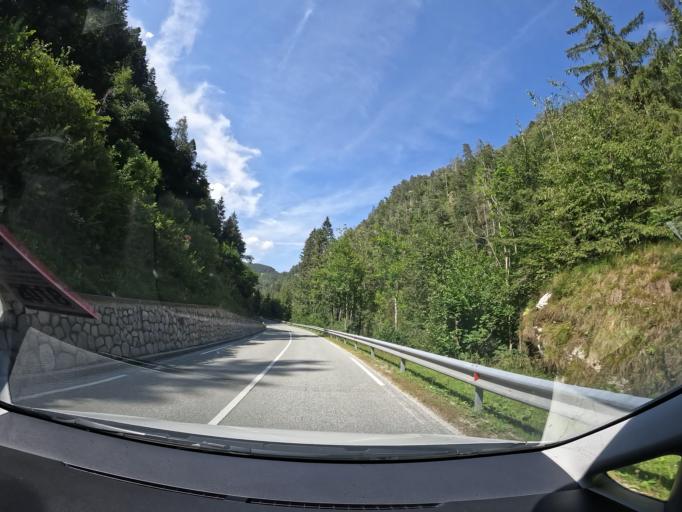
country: SI
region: Trzic
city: Bistrica pri Trzicu
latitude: 46.4280
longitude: 14.2660
